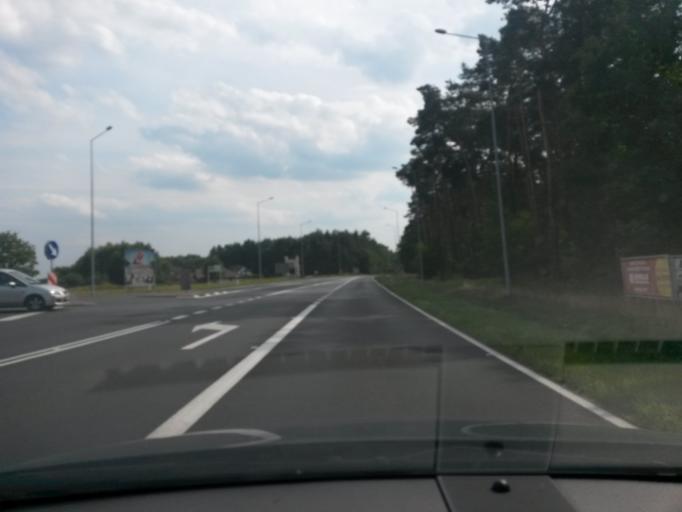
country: PL
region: Greater Poland Voivodeship
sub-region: Powiat poznanski
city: Kornik
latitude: 52.2185
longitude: 17.0735
